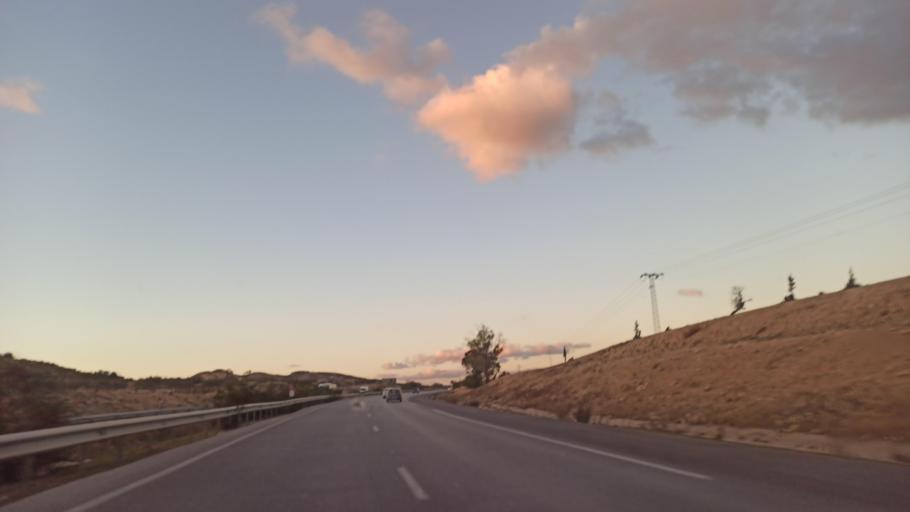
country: TN
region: Susah
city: Harqalah
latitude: 36.2280
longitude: 10.4140
